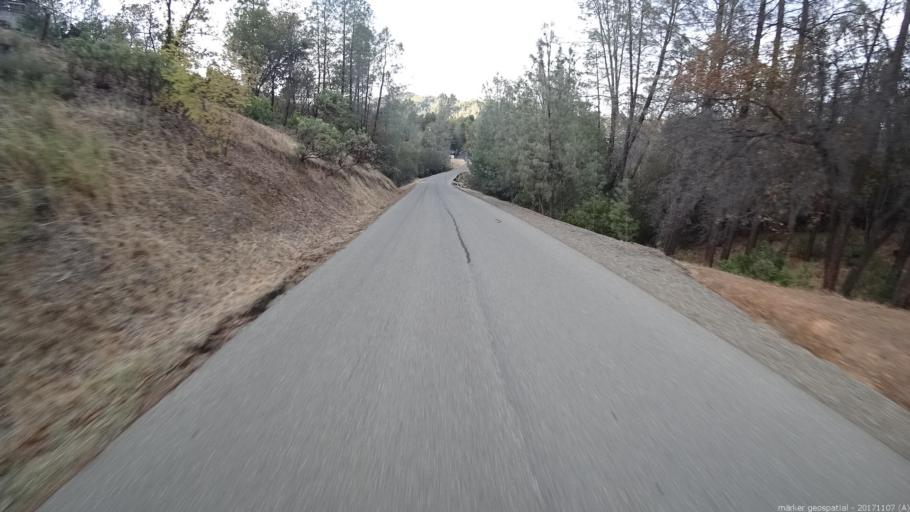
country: US
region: California
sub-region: Shasta County
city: Shasta
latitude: 40.5441
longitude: -122.4948
